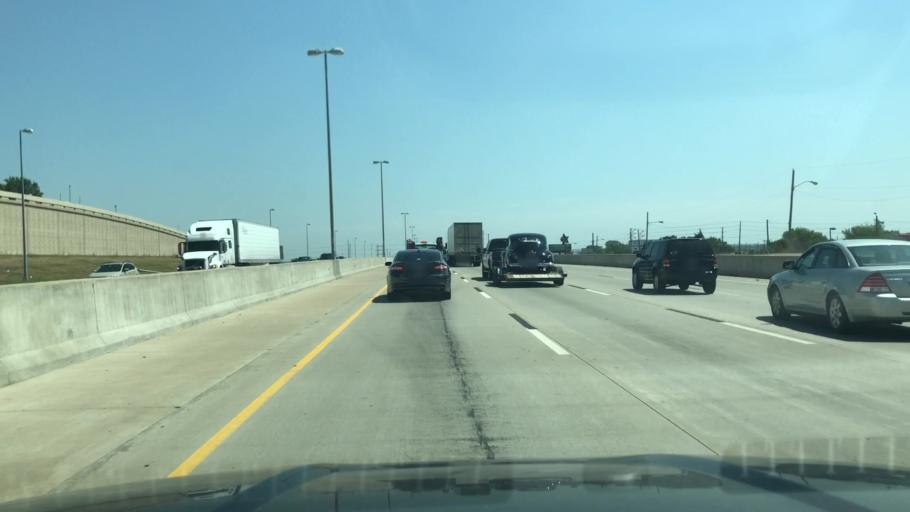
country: US
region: Oklahoma
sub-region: Tulsa County
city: Tulsa
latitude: 36.1061
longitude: -95.9070
